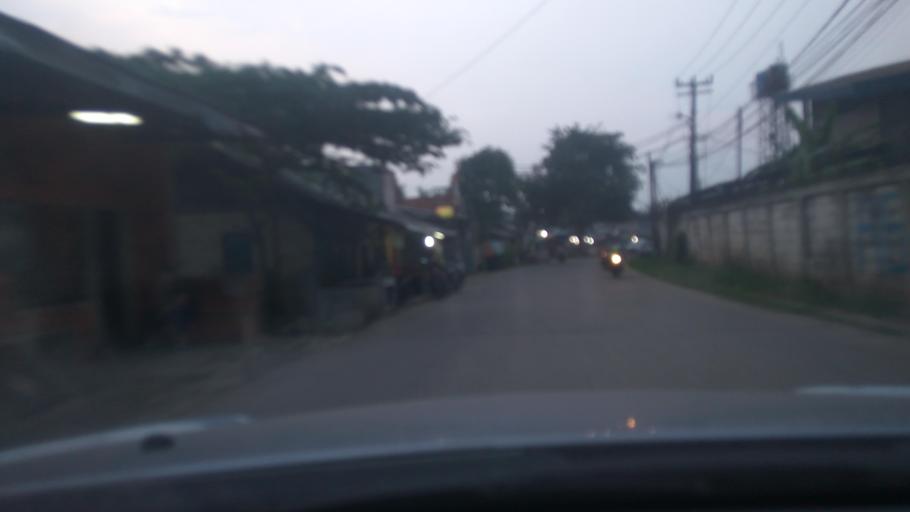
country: ID
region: West Java
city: Pamulang
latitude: -6.3696
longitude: 106.7380
